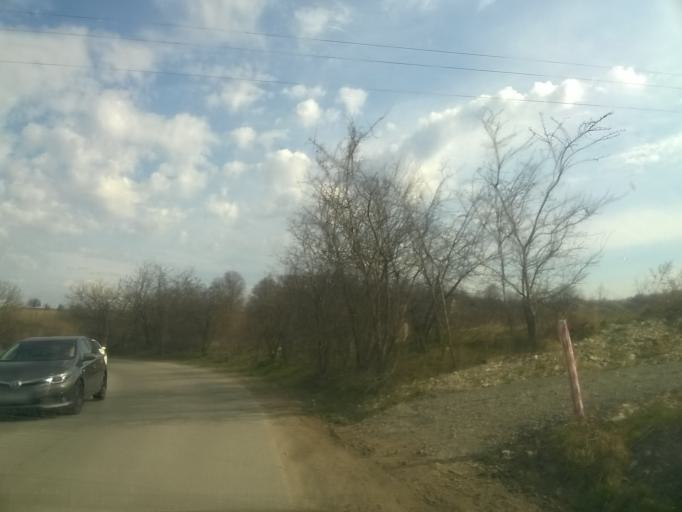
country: PL
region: Lesser Poland Voivodeship
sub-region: Powiat krakowski
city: Rzaska
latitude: 50.0865
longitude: 19.8529
